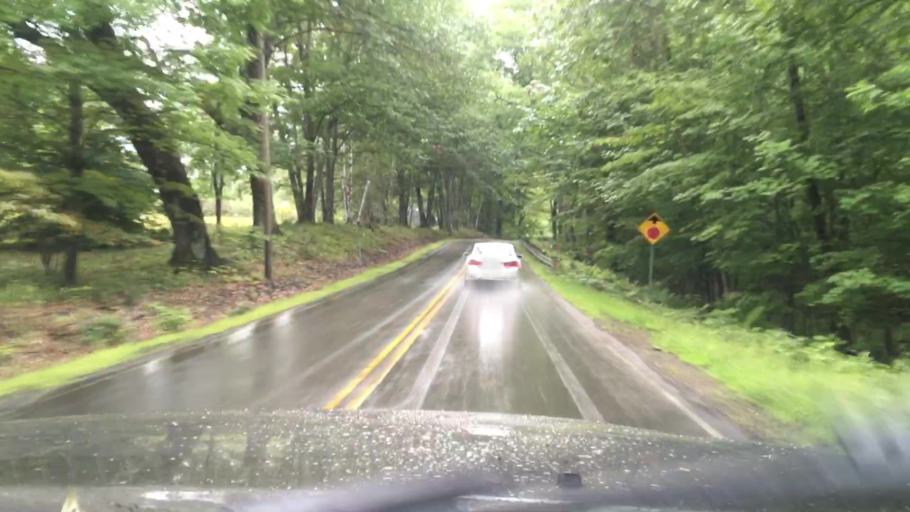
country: US
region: New Hampshire
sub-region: Belknap County
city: Meredith
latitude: 43.6583
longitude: -71.5502
